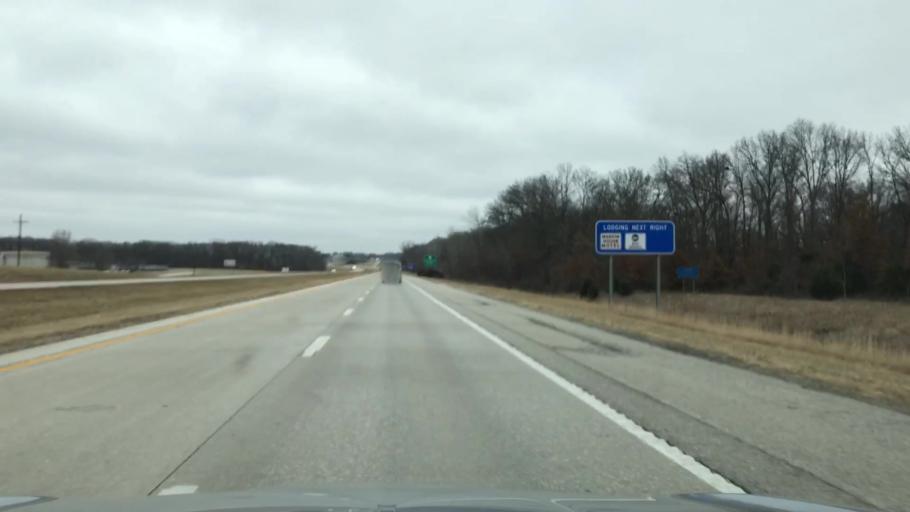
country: US
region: Missouri
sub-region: Linn County
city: Brookfield
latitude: 39.7760
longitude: -93.0912
